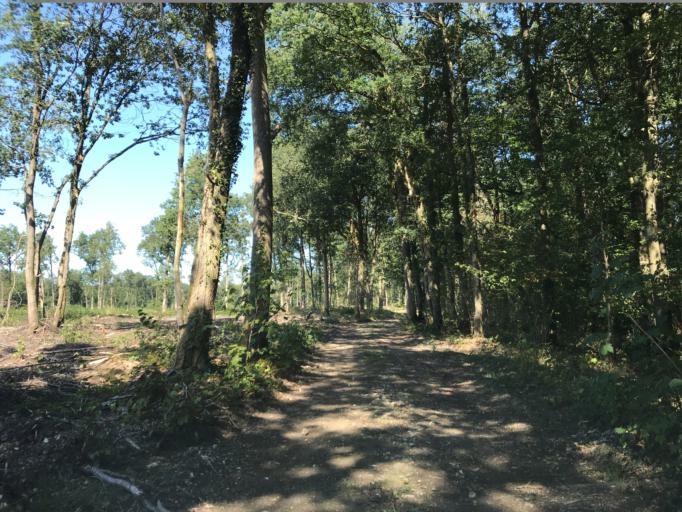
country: FR
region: Haute-Normandie
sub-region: Departement de l'Eure
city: Heudreville-sur-Eure
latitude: 49.1066
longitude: 1.2050
